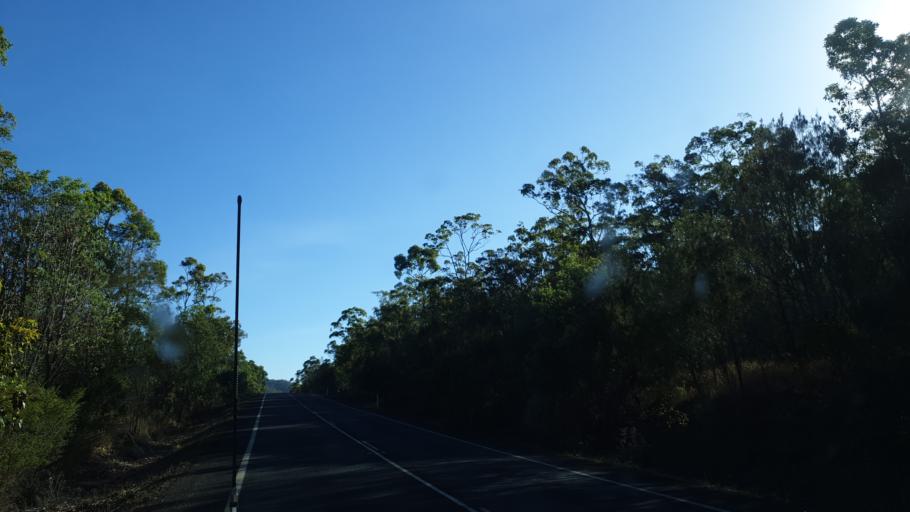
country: AU
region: Queensland
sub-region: Tablelands
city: Atherton
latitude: -17.3537
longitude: 145.4109
